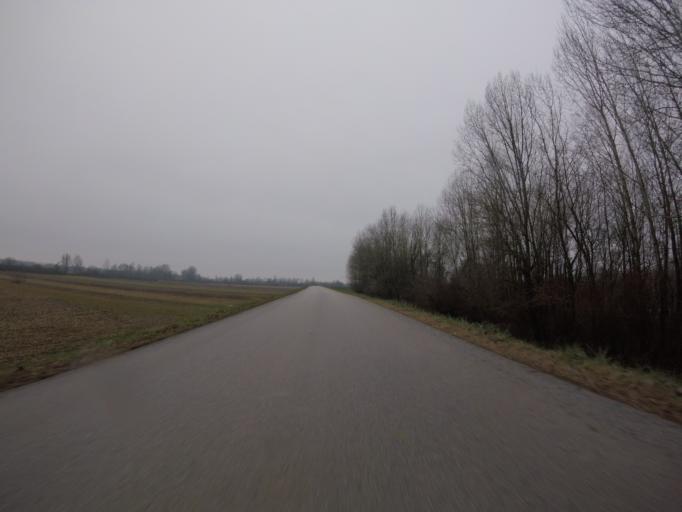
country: HR
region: Sisacko-Moslavacka
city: Lekenik
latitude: 45.6352
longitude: 16.3057
